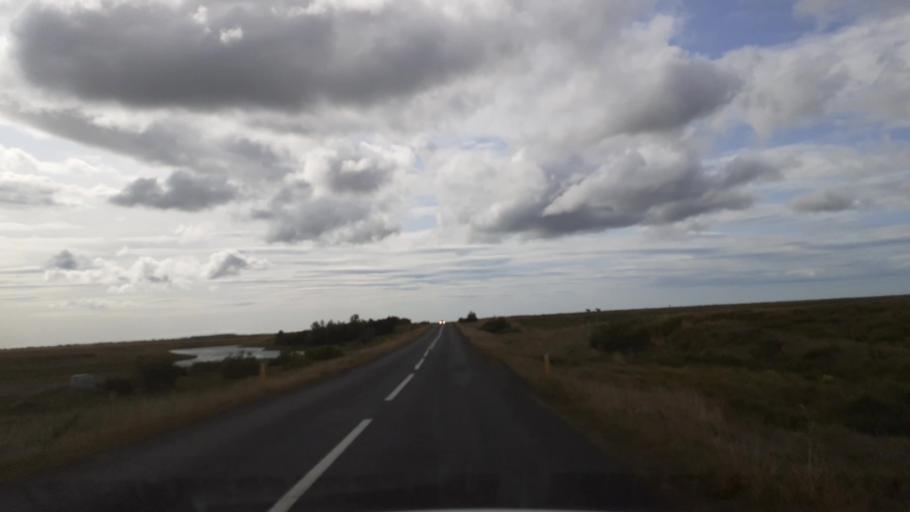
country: IS
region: South
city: Vestmannaeyjar
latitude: 63.8304
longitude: -20.4238
